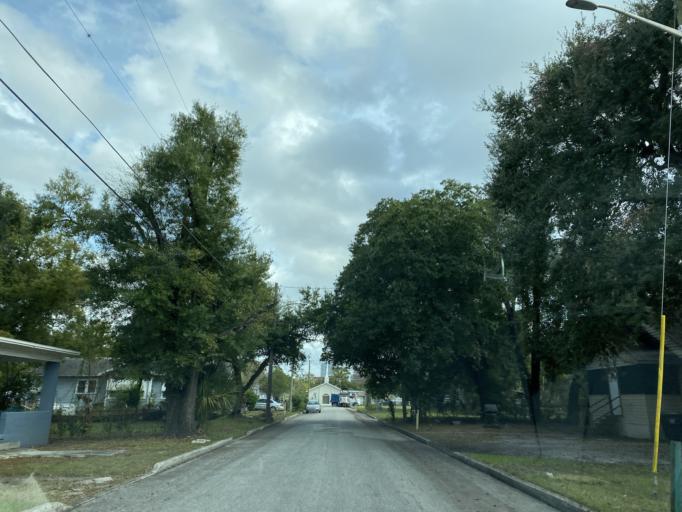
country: US
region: Florida
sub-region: Orange County
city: Orlando
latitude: 28.5449
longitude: -81.3946
